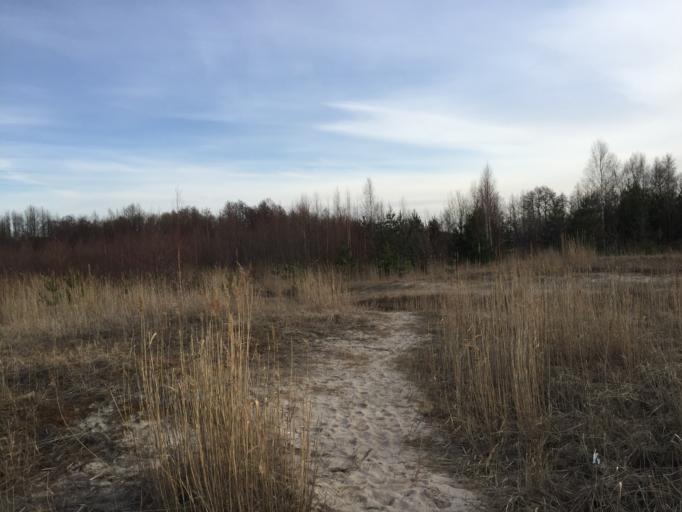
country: LV
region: Salacgrivas
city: Ainazi
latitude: 57.8689
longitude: 24.3531
